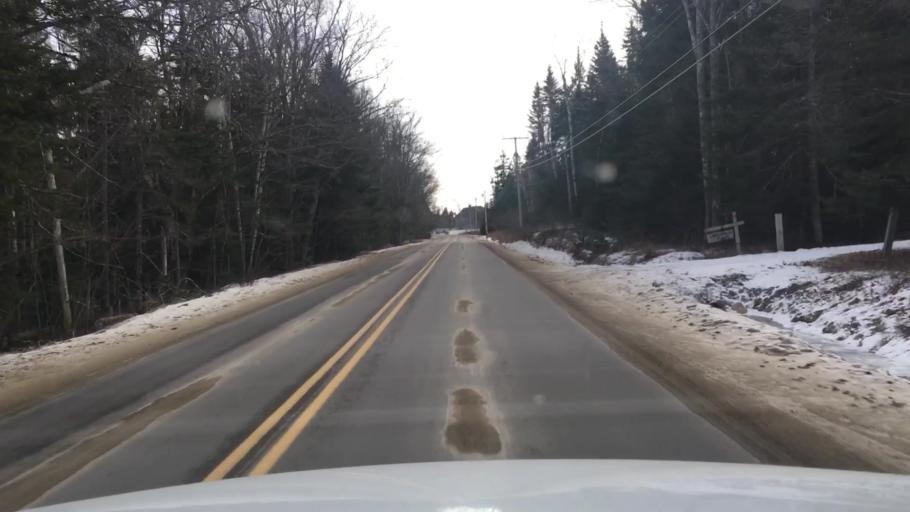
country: US
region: Maine
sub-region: Washington County
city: Jonesport
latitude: 44.6118
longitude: -67.6022
